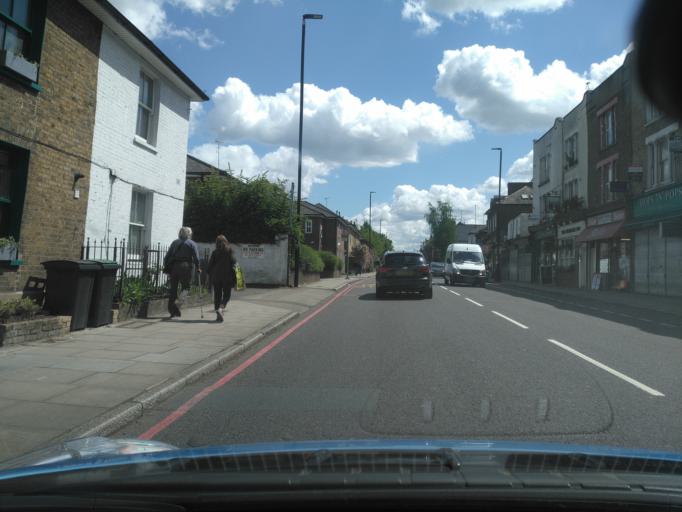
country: GB
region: England
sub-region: Greater London
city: Crouch End
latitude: 51.5786
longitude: -0.1492
